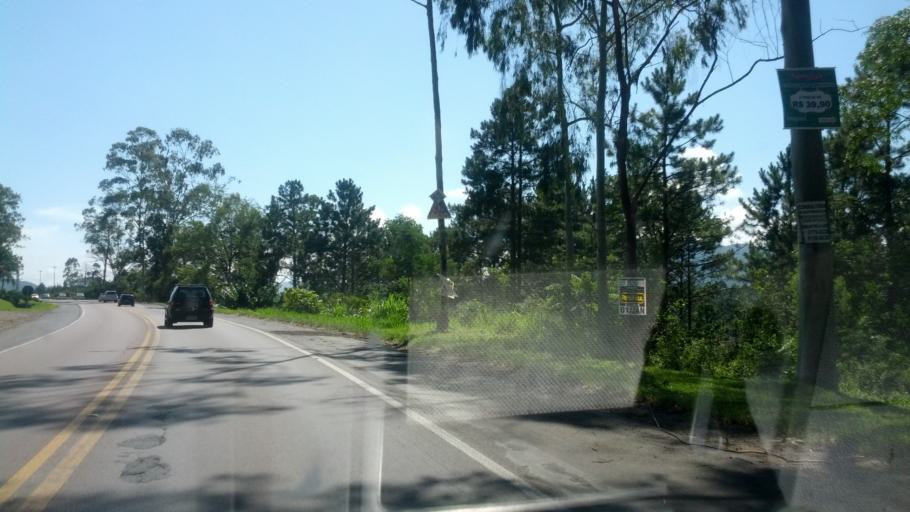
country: BR
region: Santa Catarina
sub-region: Rio Do Sul
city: Rio do Sul
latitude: -27.1881
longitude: -49.6099
